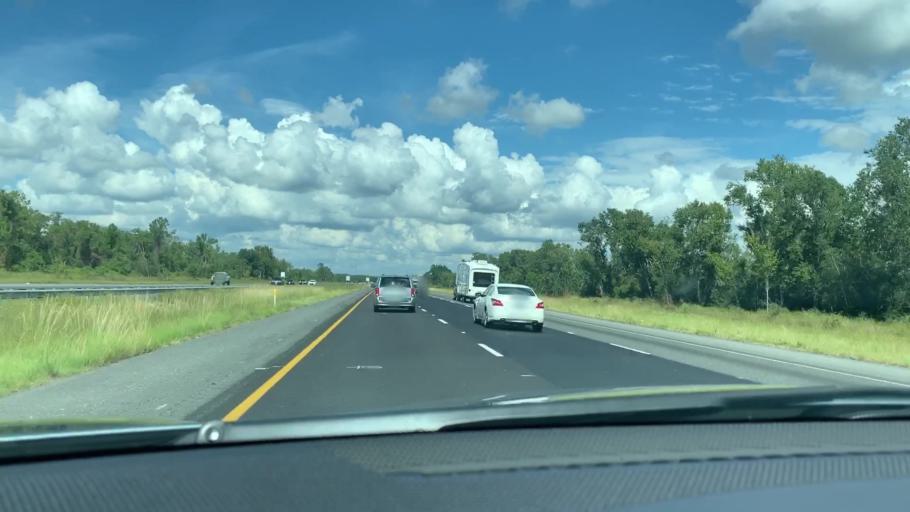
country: US
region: Georgia
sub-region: Camden County
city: Woodbine
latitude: 31.0221
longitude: -81.6574
